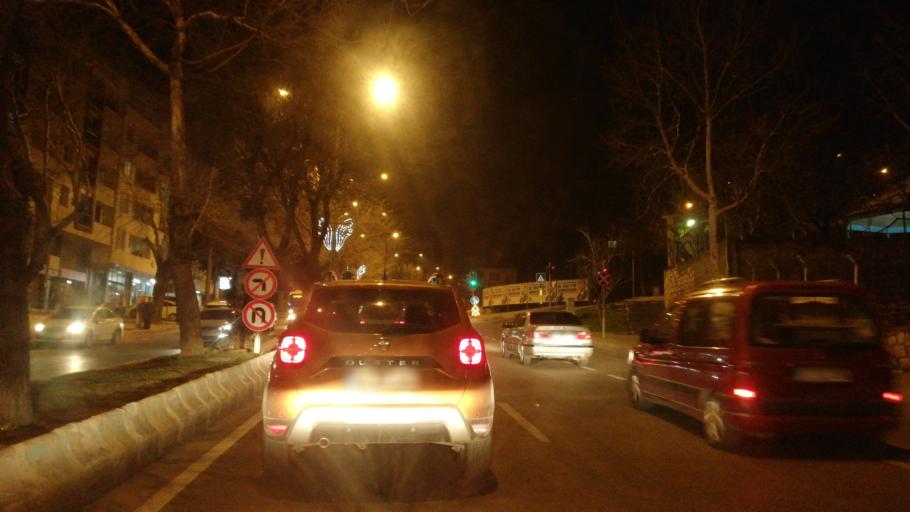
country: TR
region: Kahramanmaras
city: Kahramanmaras
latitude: 37.5775
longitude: 36.9172
